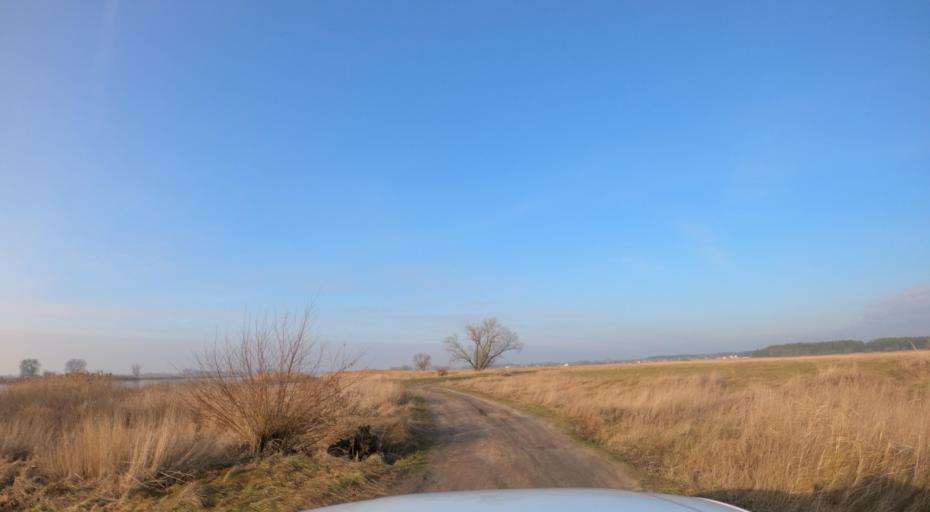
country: PL
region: Lubusz
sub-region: Powiat gorzowski
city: Kostrzyn nad Odra
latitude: 52.6104
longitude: 14.5991
